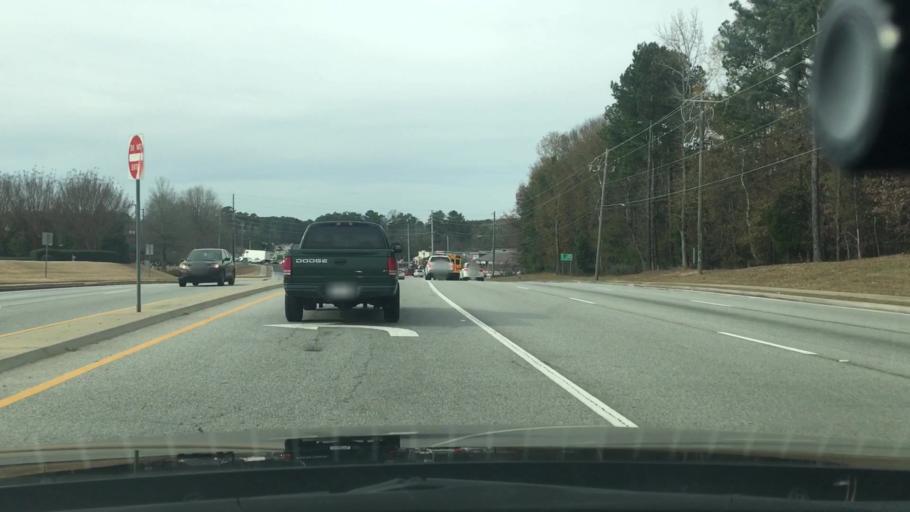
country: US
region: Georgia
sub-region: Fayette County
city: Peachtree City
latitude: 33.3958
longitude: -84.5888
